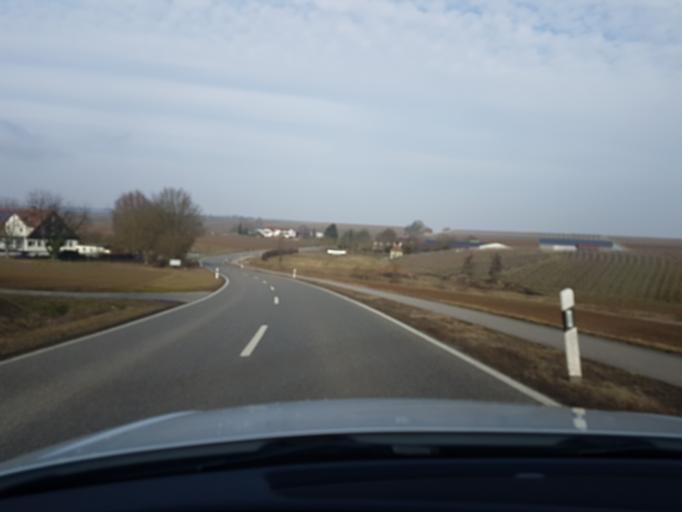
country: DE
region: Baden-Wuerttemberg
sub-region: Regierungsbezirk Stuttgart
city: Lauffen am Neckar
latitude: 49.0921
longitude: 9.1400
